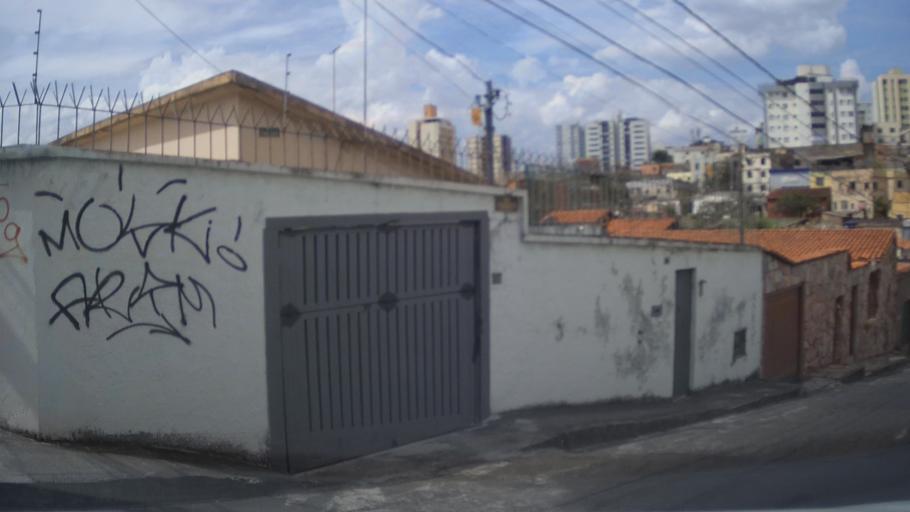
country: BR
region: Minas Gerais
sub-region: Belo Horizonte
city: Belo Horizonte
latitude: -19.8878
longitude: -43.9370
